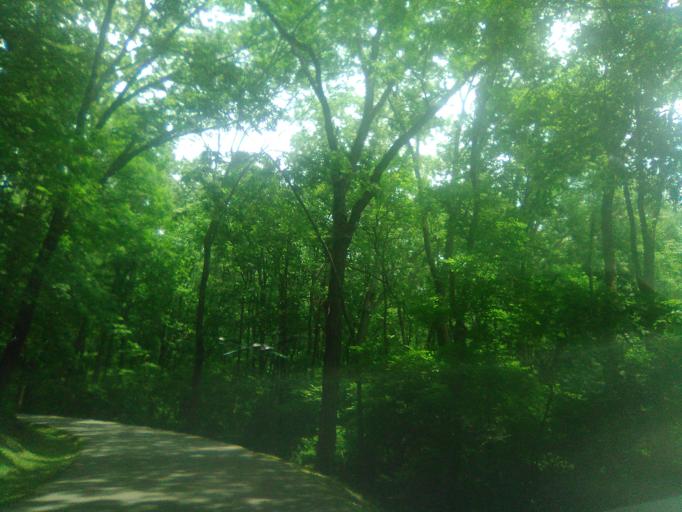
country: US
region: Tennessee
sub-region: Davidson County
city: Belle Meade
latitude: 36.0809
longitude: -86.8743
